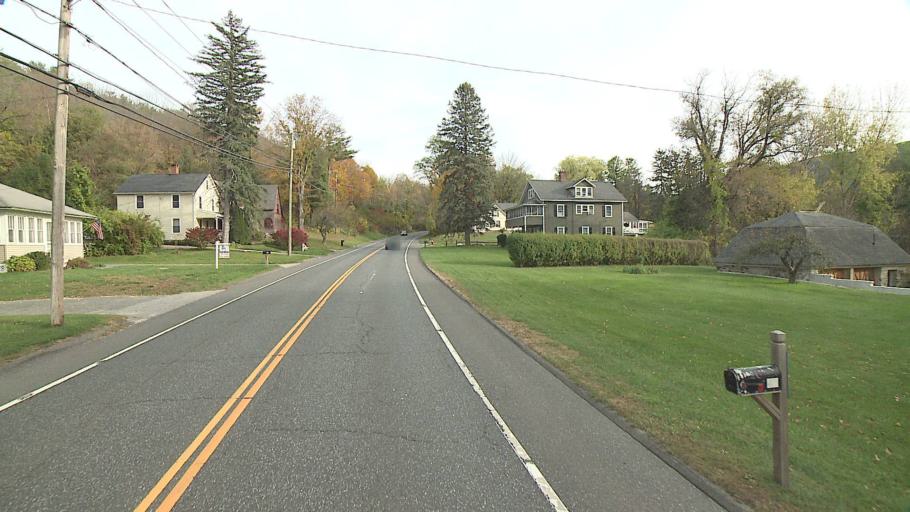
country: US
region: Connecticut
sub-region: Litchfield County
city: Canaan
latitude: 42.0228
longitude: -73.3187
